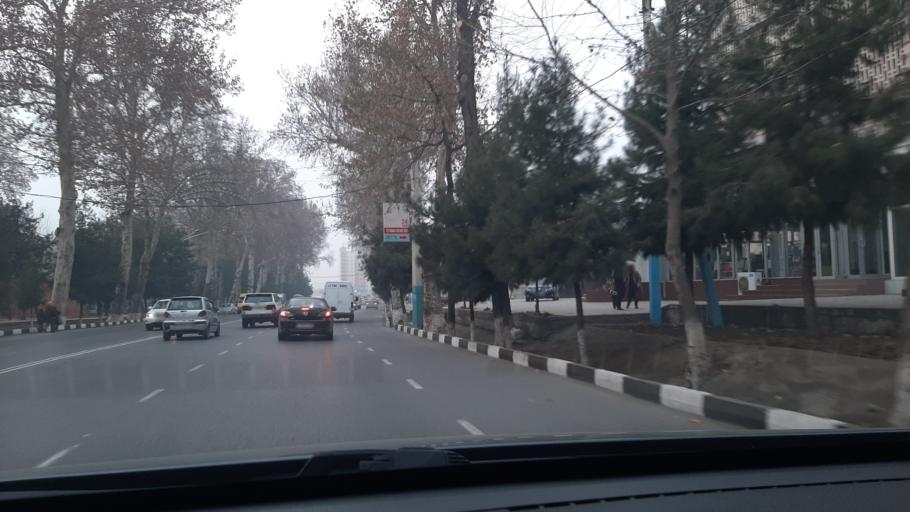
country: TJ
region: Viloyati Sughd
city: Khujand
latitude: 40.2693
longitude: 69.6467
